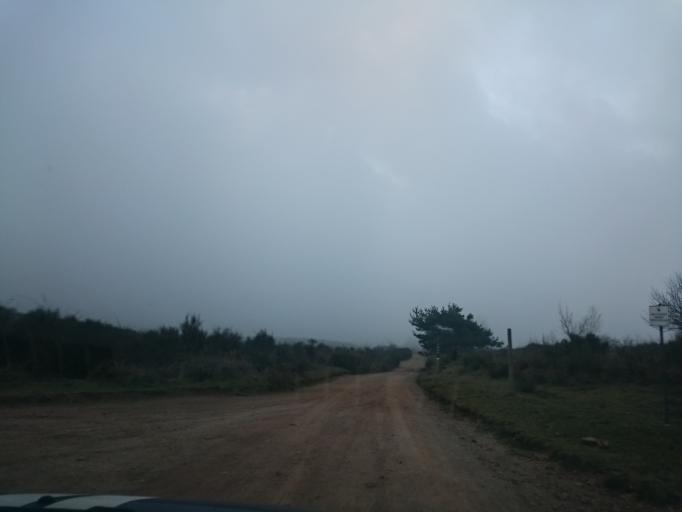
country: ES
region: Catalonia
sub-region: Provincia de Barcelona
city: Tagamanent
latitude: 41.7647
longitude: 2.3331
